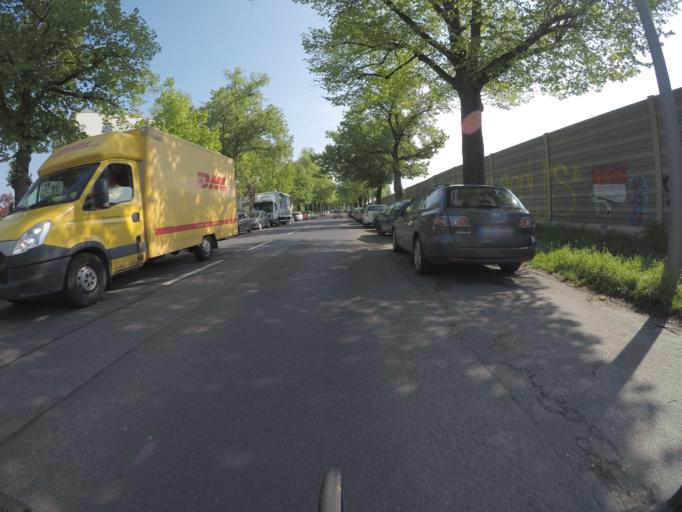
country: DE
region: Berlin
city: Heinersdorf
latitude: 52.5745
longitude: 13.4240
